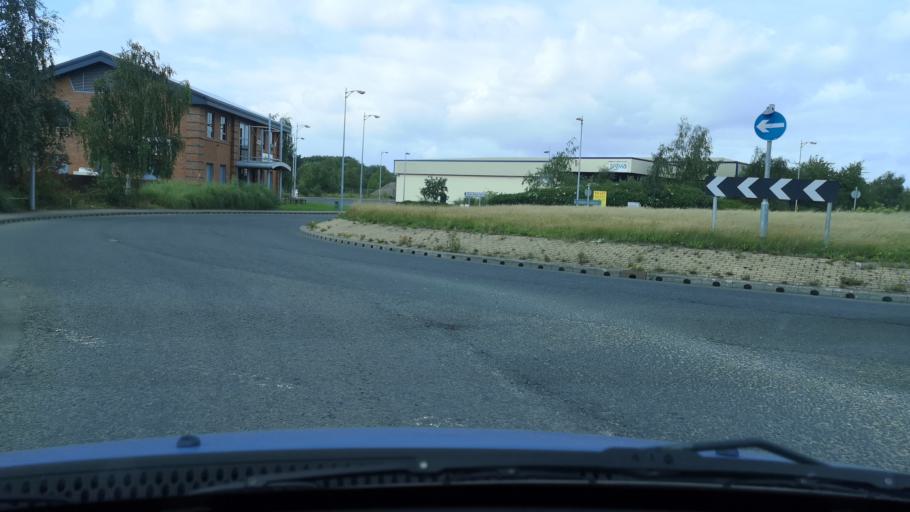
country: GB
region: England
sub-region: City and Borough of Wakefield
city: Castleford
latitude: 53.7105
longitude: -1.3449
